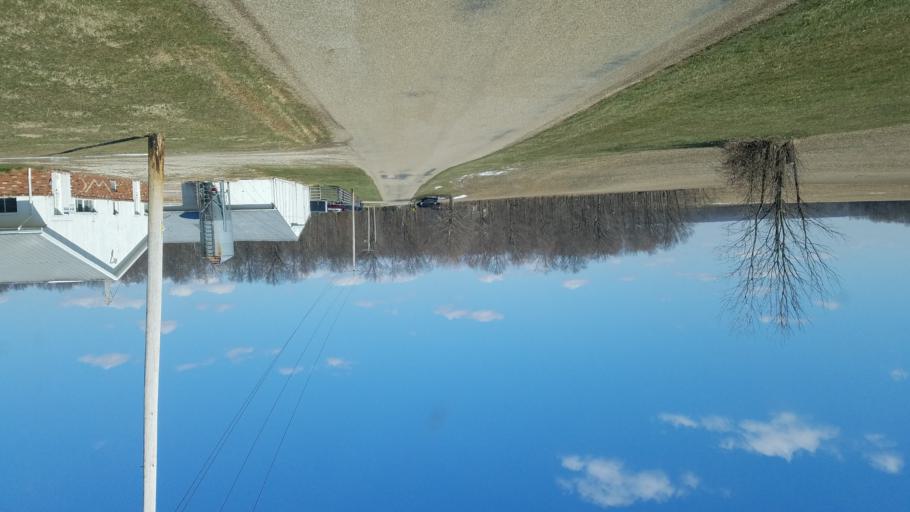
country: US
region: Ohio
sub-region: Knox County
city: Fredericktown
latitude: 40.4427
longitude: -82.6288
